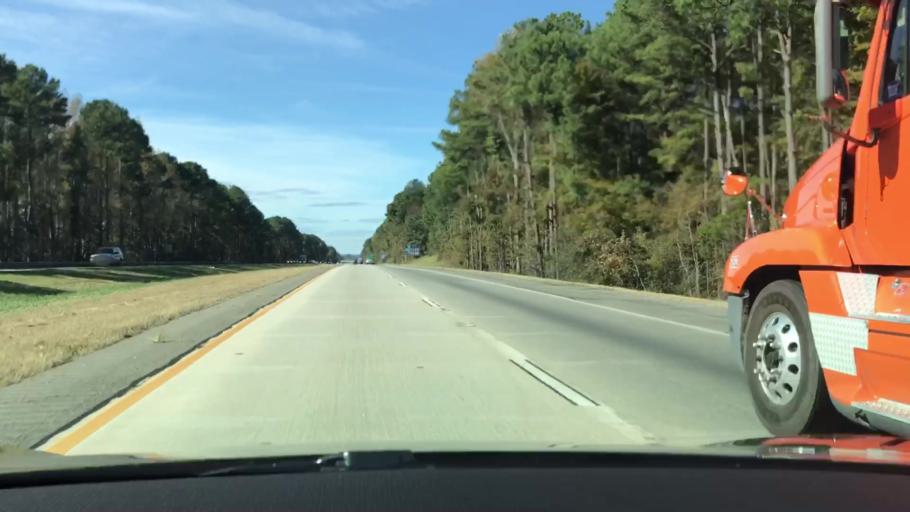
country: US
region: Georgia
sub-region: Greene County
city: Greensboro
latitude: 33.5475
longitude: -83.1750
